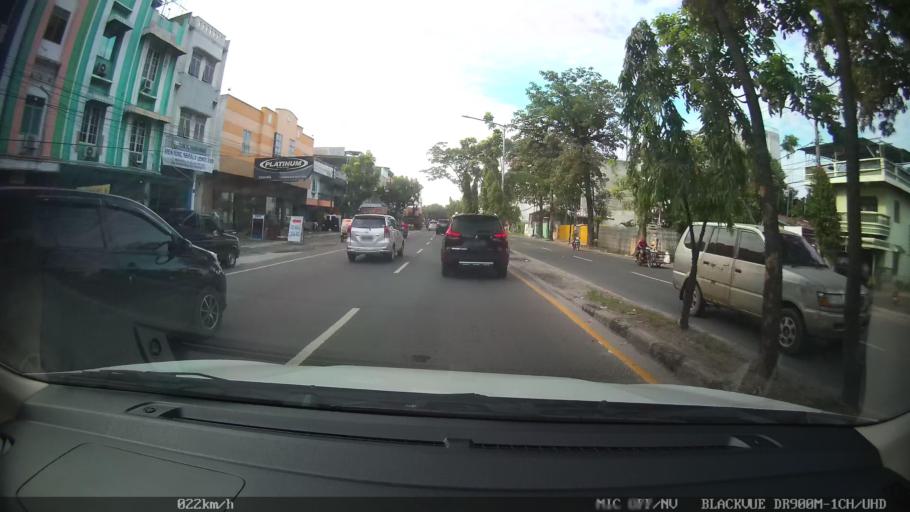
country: ID
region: North Sumatra
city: Medan
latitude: 3.6305
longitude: 98.6812
